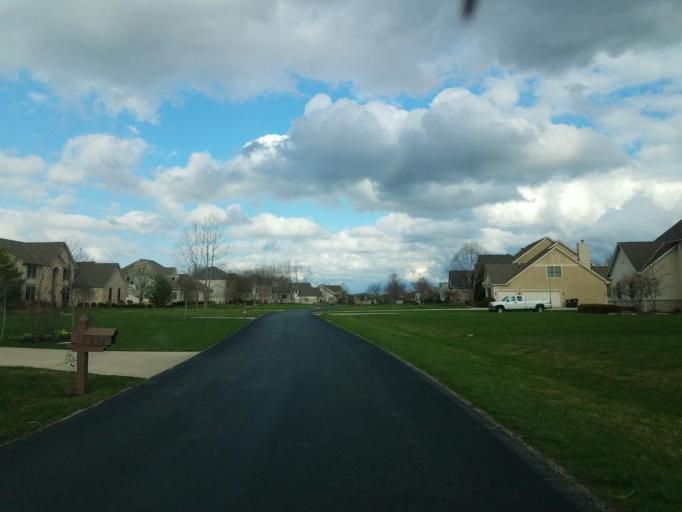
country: US
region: Ohio
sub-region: Delaware County
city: Powell
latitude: 40.1743
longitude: -83.0761
